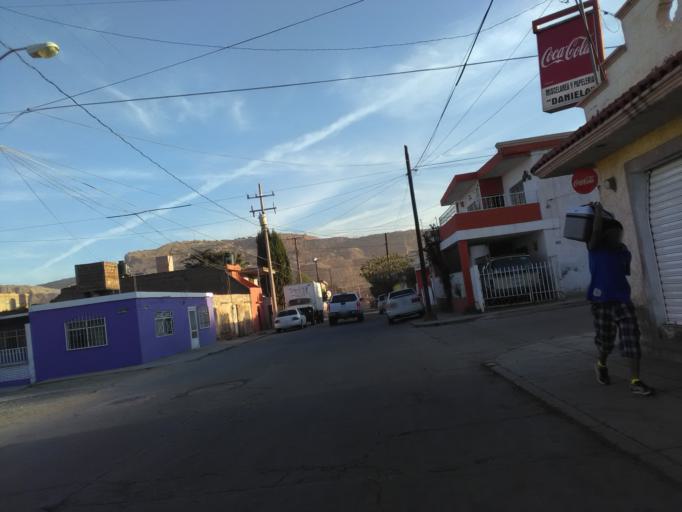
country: MX
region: Durango
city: Victoria de Durango
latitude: 24.0446
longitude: -104.6687
